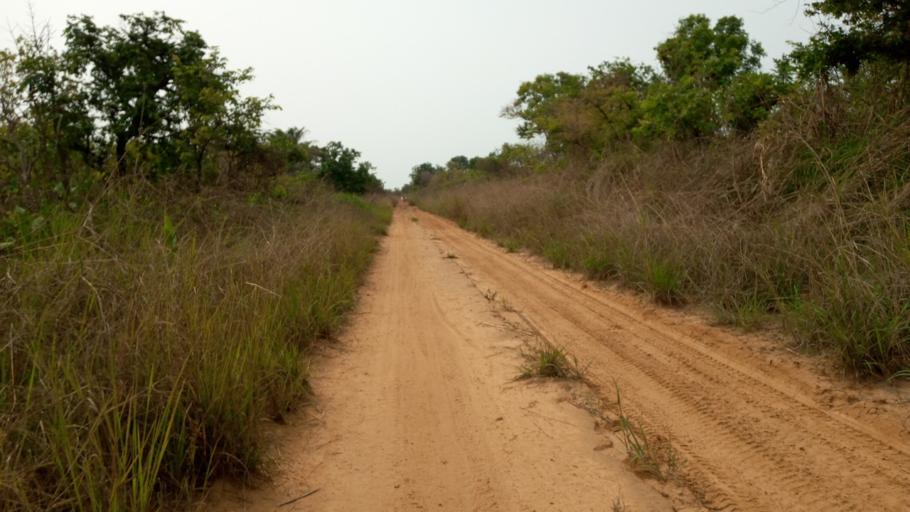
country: CD
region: Bandundu
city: Bandundu
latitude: -3.4681
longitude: 17.7757
